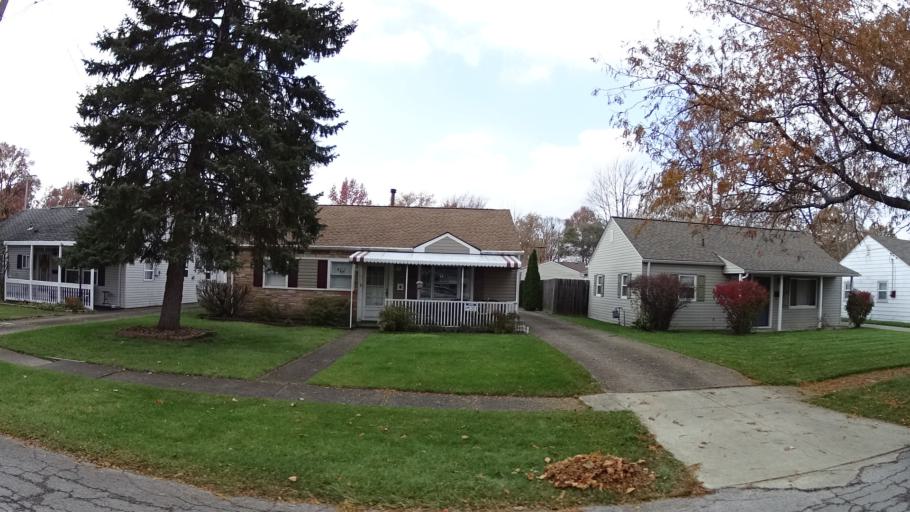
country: US
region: Ohio
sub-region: Lorain County
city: Elyria
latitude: 41.3819
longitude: -82.0870
